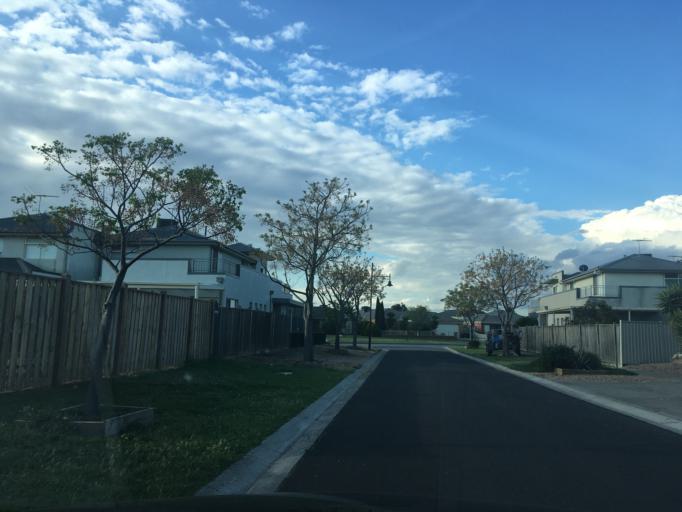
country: AU
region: Victoria
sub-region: Wyndham
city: Hoppers Crossing
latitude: -37.8825
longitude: 144.7242
